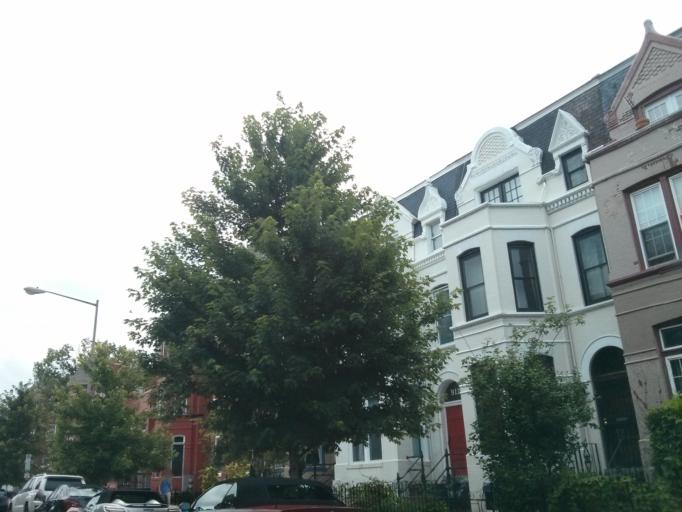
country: US
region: Washington, D.C.
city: Washington, D.C.
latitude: 38.9156
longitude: -77.0249
